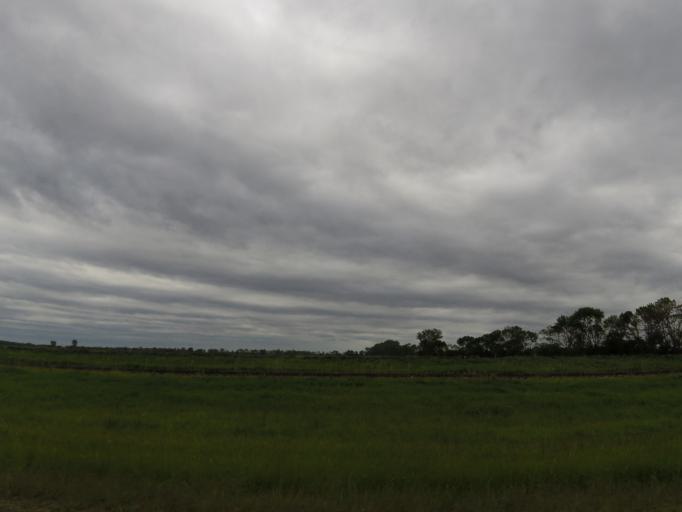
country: US
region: North Dakota
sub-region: Walsh County
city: Grafton
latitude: 48.5652
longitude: -97.4479
